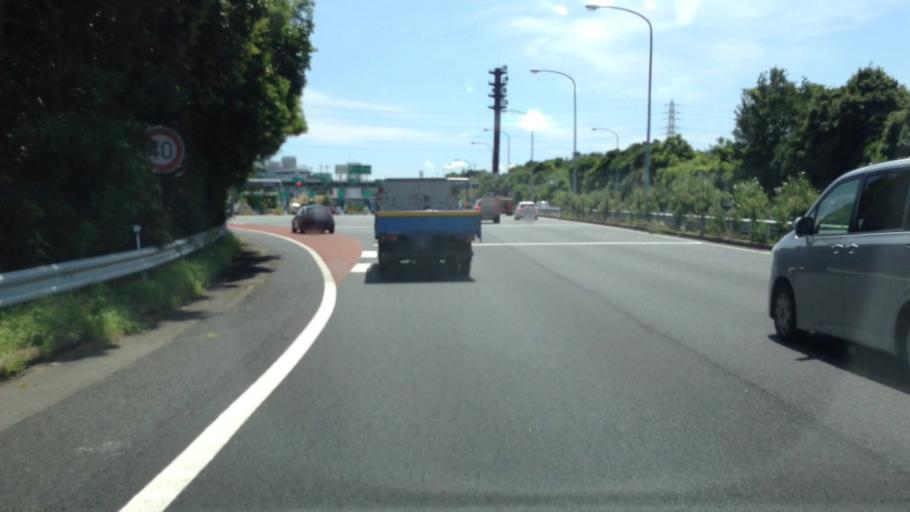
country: JP
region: Kanagawa
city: Yokohama
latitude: 35.4857
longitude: 139.5930
